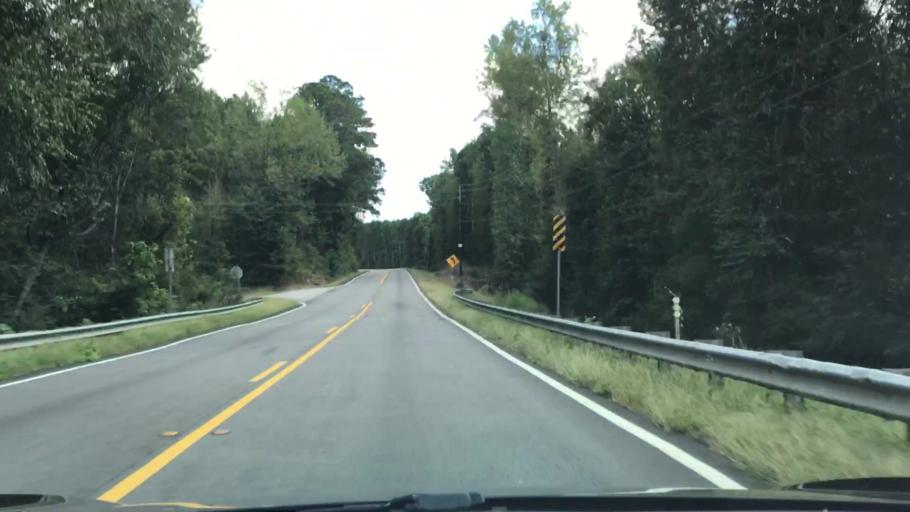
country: US
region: Georgia
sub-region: Greene County
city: Greensboro
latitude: 33.5612
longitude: -83.1397
